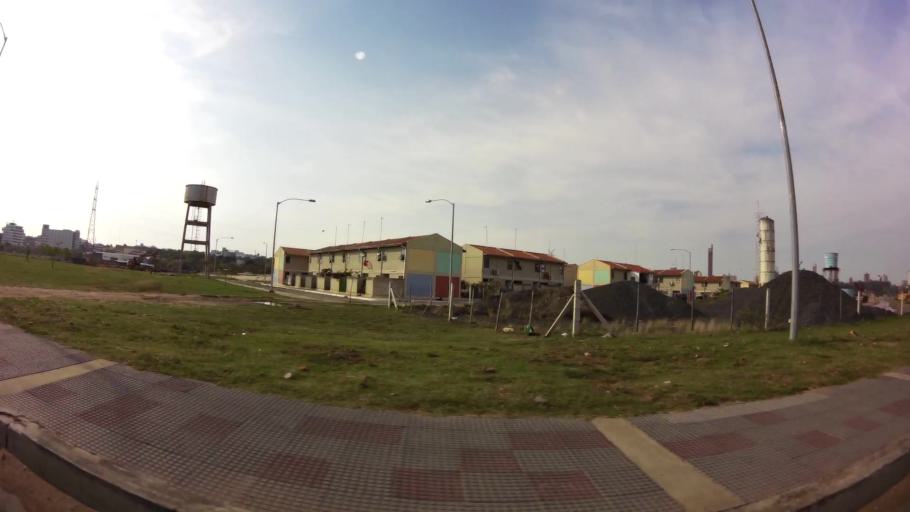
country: PY
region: Asuncion
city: Asuncion
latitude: -25.2710
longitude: -57.6140
